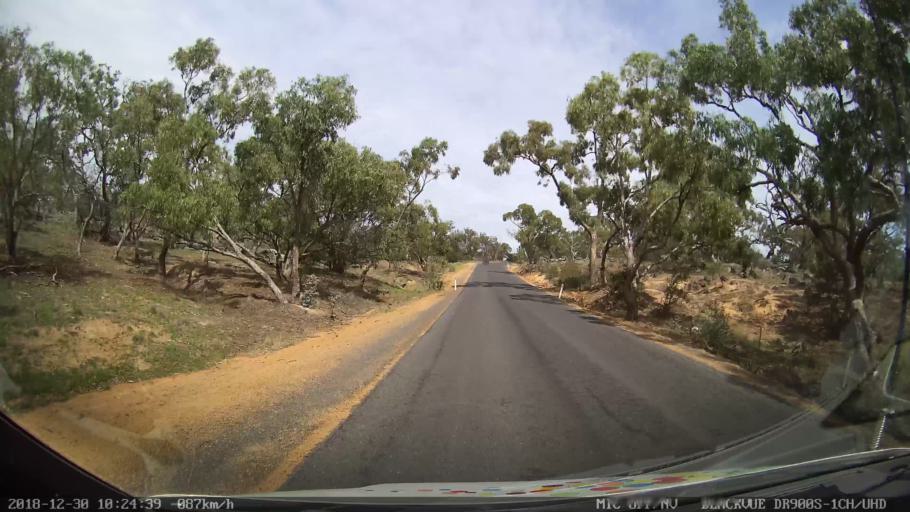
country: AU
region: New South Wales
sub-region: Snowy River
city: Berridale
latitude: -36.5311
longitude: 148.9660
